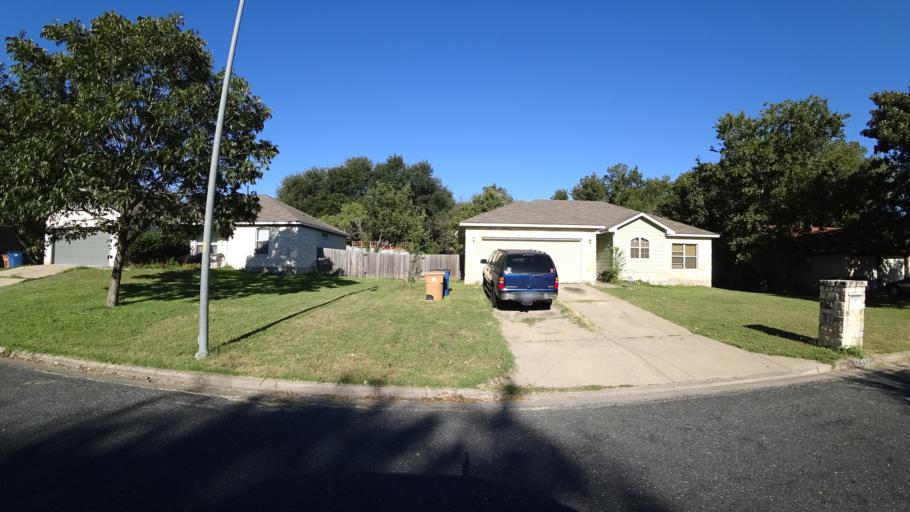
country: US
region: Texas
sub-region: Travis County
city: Hornsby Bend
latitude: 30.3117
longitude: -97.6516
